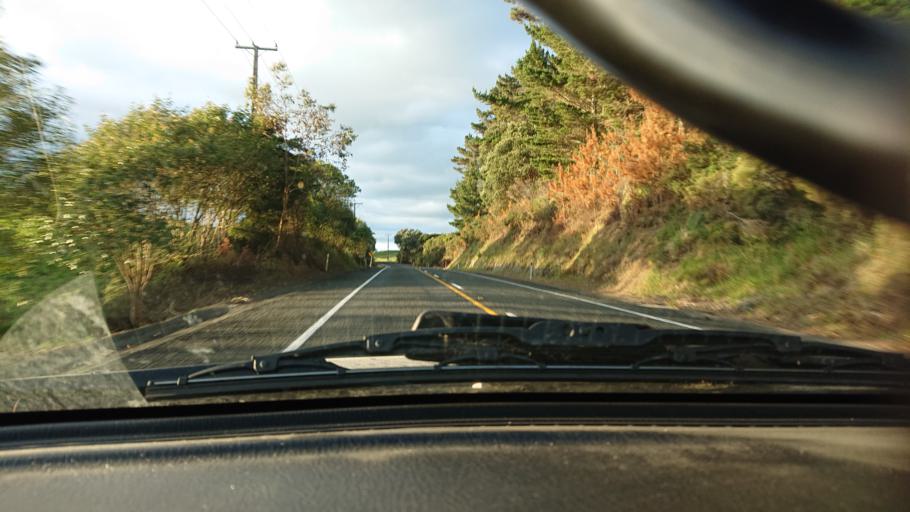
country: NZ
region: Auckland
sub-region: Auckland
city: Parakai
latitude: -36.5021
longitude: 174.4542
